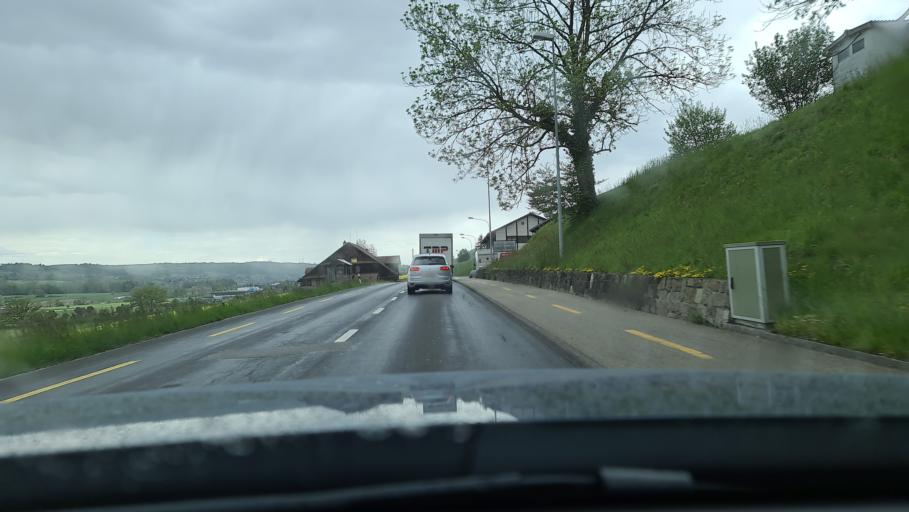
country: CH
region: Lucerne
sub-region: Sursee District
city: Bueron
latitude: 47.2192
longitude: 8.0899
